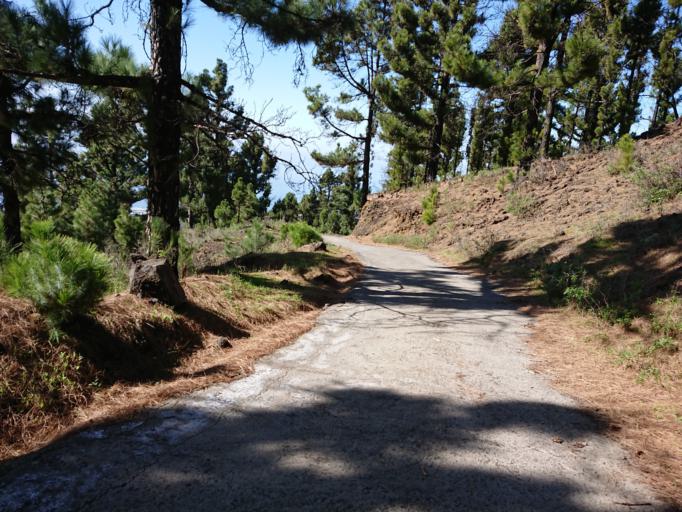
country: ES
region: Canary Islands
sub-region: Provincia de Santa Cruz de Tenerife
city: El Paso
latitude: 28.6071
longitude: -17.8639
